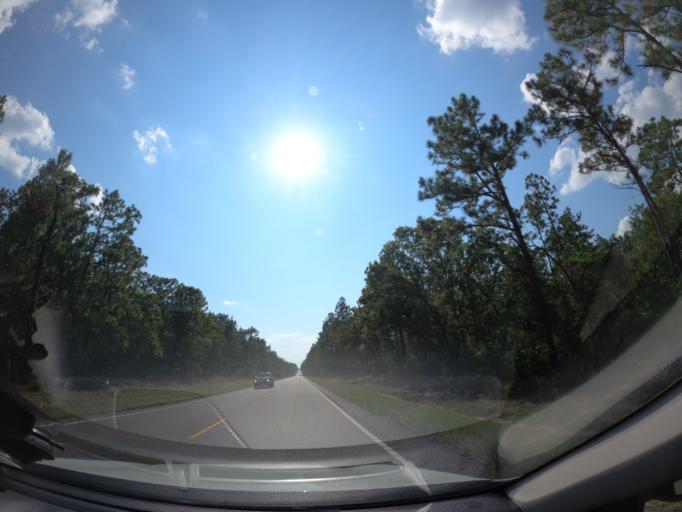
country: US
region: South Carolina
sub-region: Aiken County
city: New Ellenton
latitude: 33.3876
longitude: -81.5905
